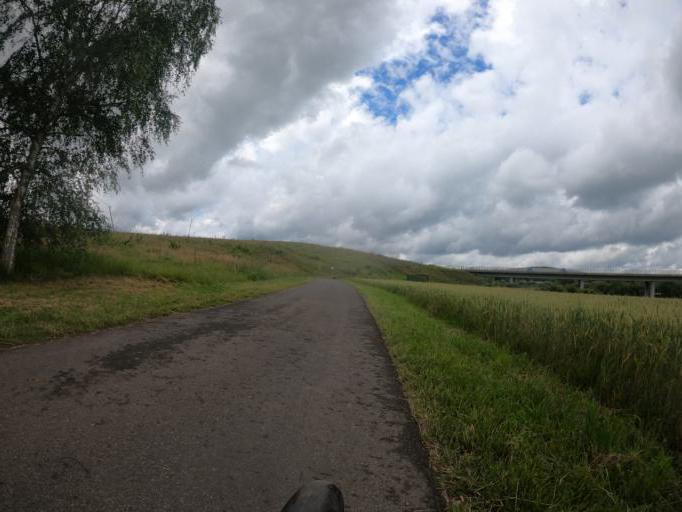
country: DE
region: Hesse
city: Hessisch Lichtenau
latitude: 51.1925
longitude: 9.7799
